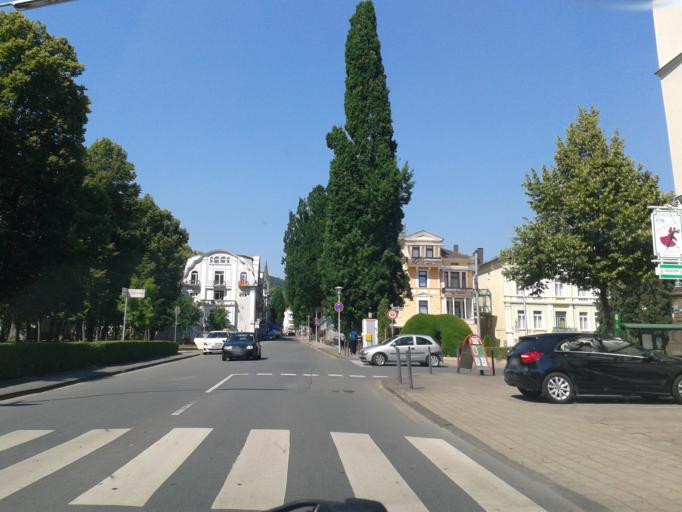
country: DE
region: Lower Saxony
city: Bad Pyrmont
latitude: 51.9835
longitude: 9.2534
